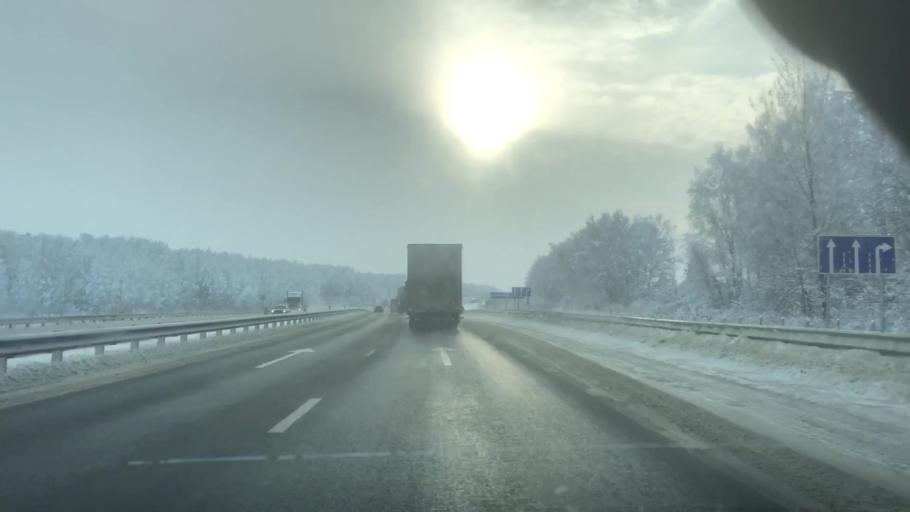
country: RU
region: Tula
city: Venev
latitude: 54.5180
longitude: 38.1697
